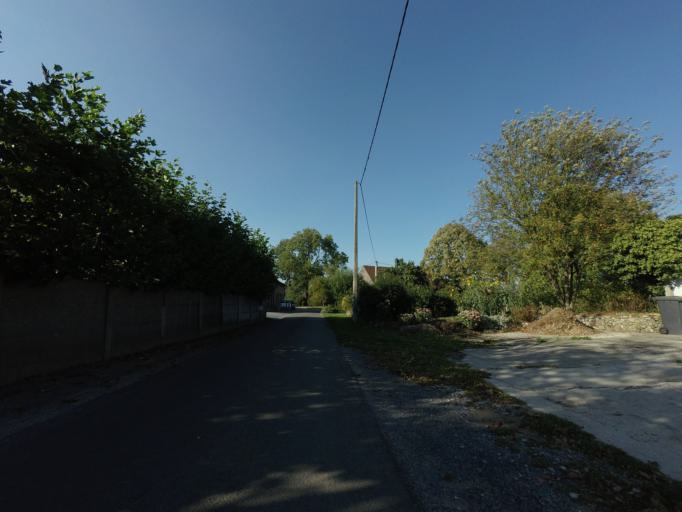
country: BE
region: Flanders
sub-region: Provincie Vlaams-Brabant
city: Kampenhout
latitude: 50.9370
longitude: 4.5932
